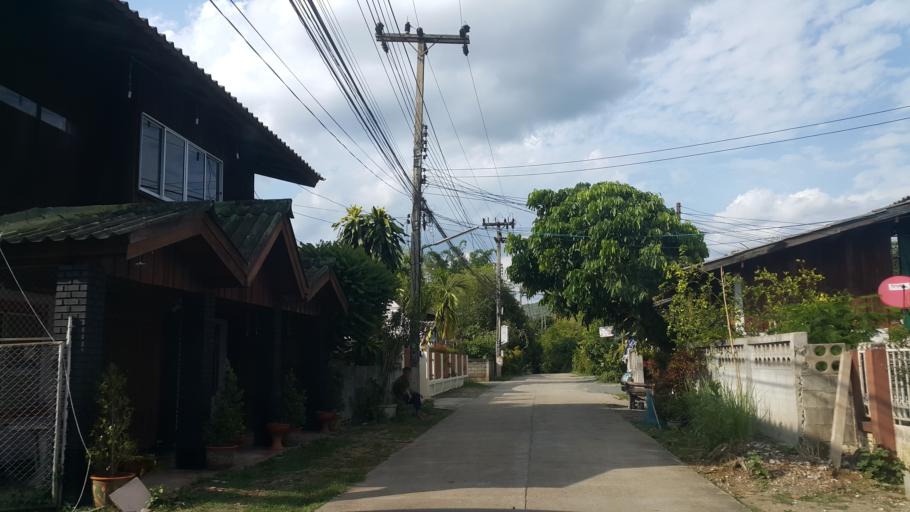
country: TH
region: Chiang Mai
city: Mae On
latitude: 18.7964
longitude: 99.2598
